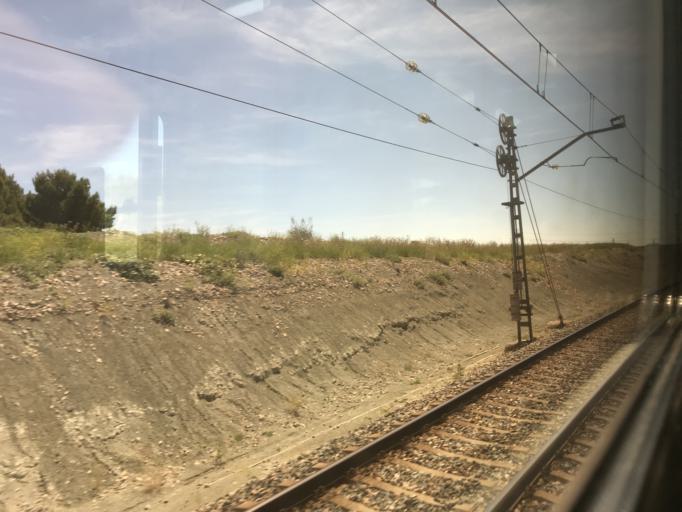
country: ES
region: Madrid
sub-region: Provincia de Madrid
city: Pinto
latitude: 40.2265
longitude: -3.6915
